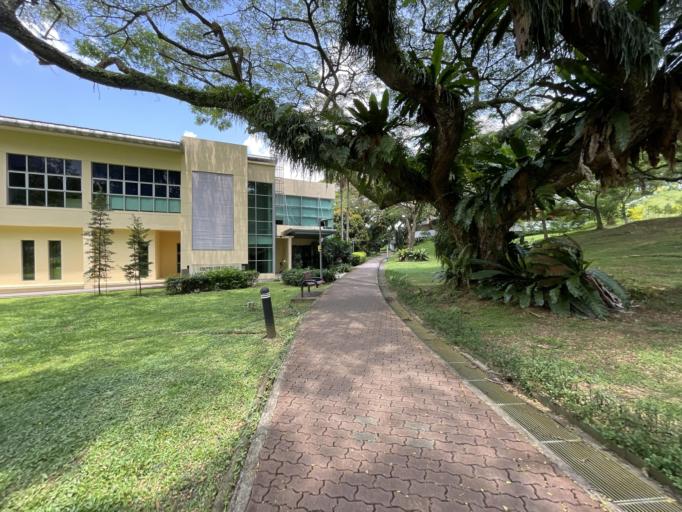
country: SG
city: Singapore
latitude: 1.2970
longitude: 103.7718
